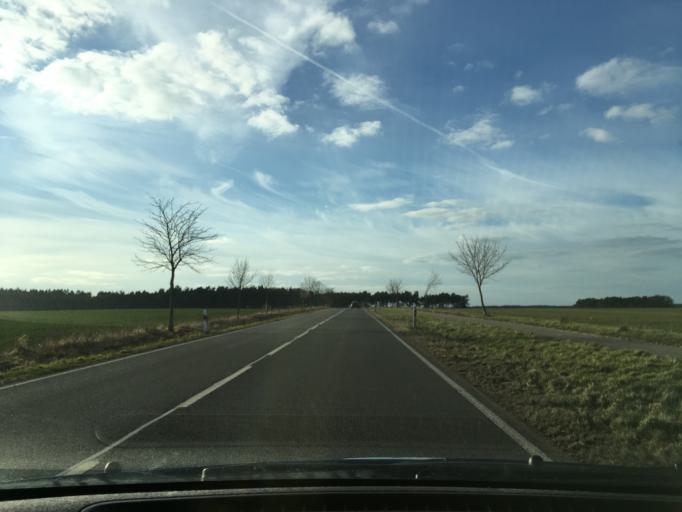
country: DE
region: Saxony-Anhalt
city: Luftkurort Arendsee
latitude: 52.8836
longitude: 11.5516
